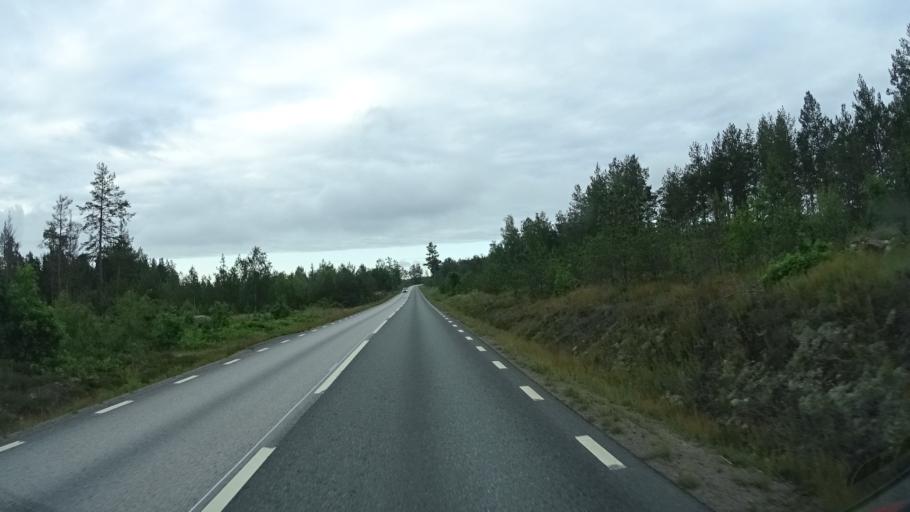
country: SE
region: Kalmar
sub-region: Oskarshamns Kommun
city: Oskarshamn
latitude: 57.2960
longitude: 16.2915
